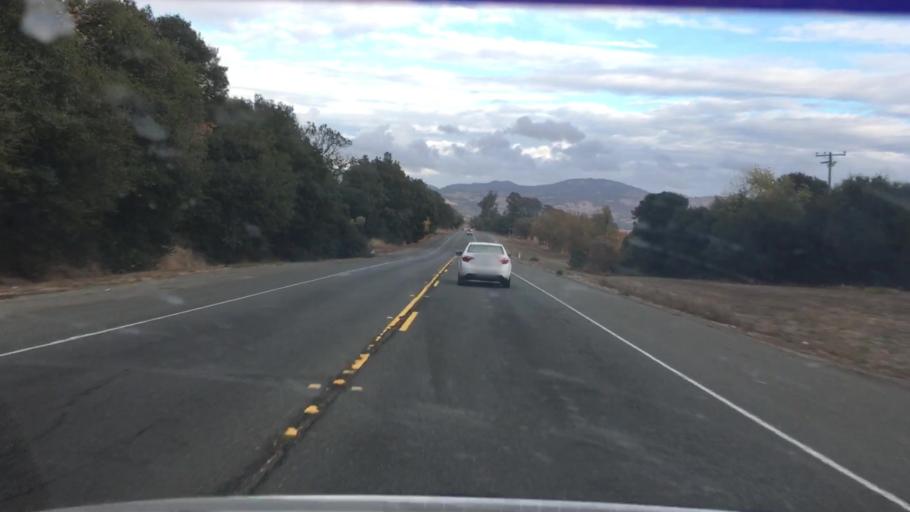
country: US
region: California
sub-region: Napa County
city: Napa
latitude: 38.2571
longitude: -122.3220
